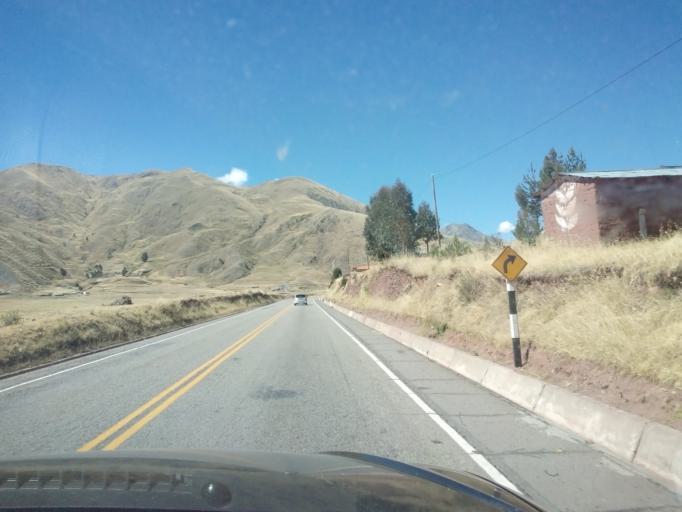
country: PE
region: Cusco
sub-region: Provincia de Canchis
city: Marangani
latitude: -14.4092
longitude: -71.1206
